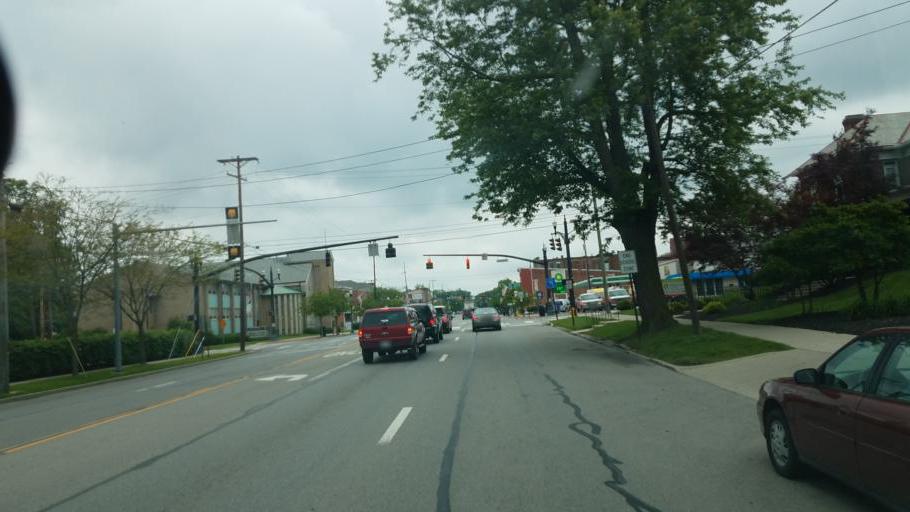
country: US
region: Ohio
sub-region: Delaware County
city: Delaware
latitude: 40.2987
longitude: -83.0653
